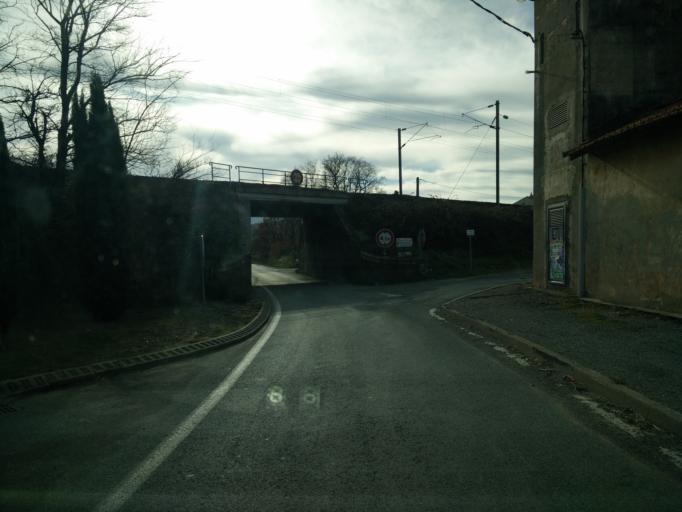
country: FR
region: Provence-Alpes-Cote d'Azur
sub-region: Departement du Var
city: Roquebrune-sur-Argens
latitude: 43.4571
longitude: 6.6340
